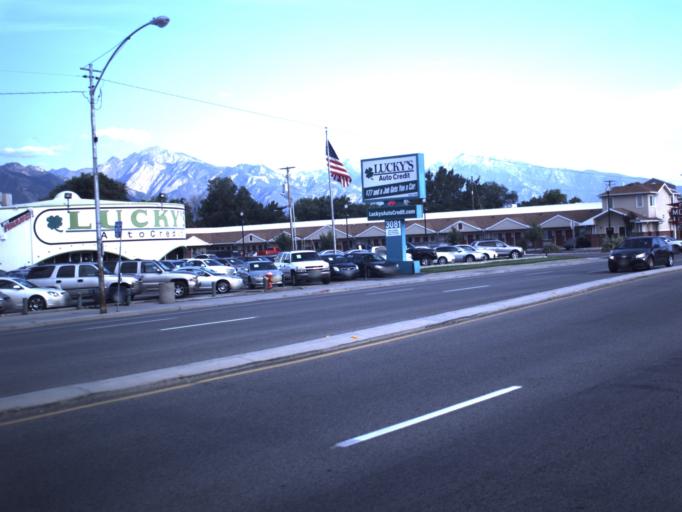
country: US
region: Utah
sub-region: Salt Lake County
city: South Salt Lake
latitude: 40.7043
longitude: -111.8884
